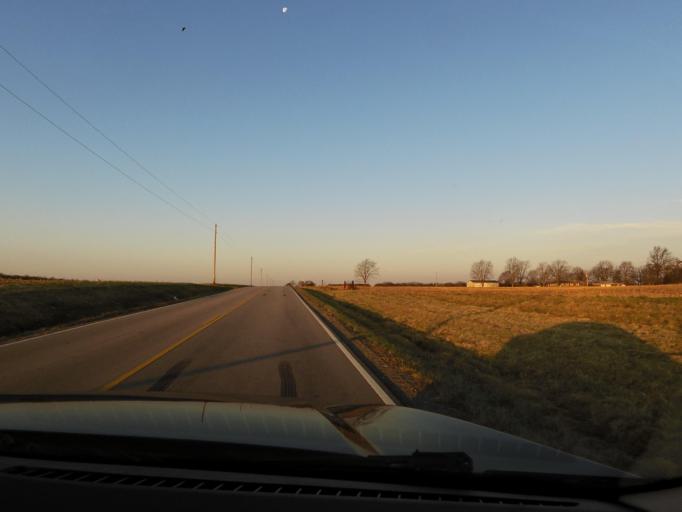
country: US
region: Illinois
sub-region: Marion County
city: Salem
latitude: 38.7586
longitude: -88.9081
